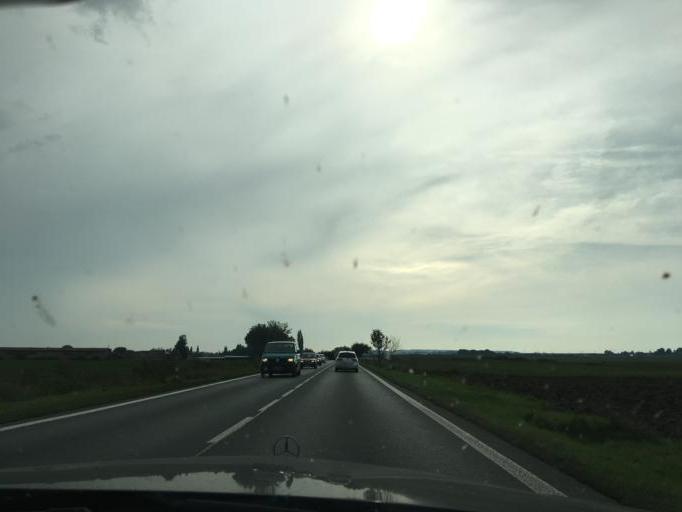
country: CZ
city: Predmerice nad Labem
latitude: 50.2851
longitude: 15.8229
